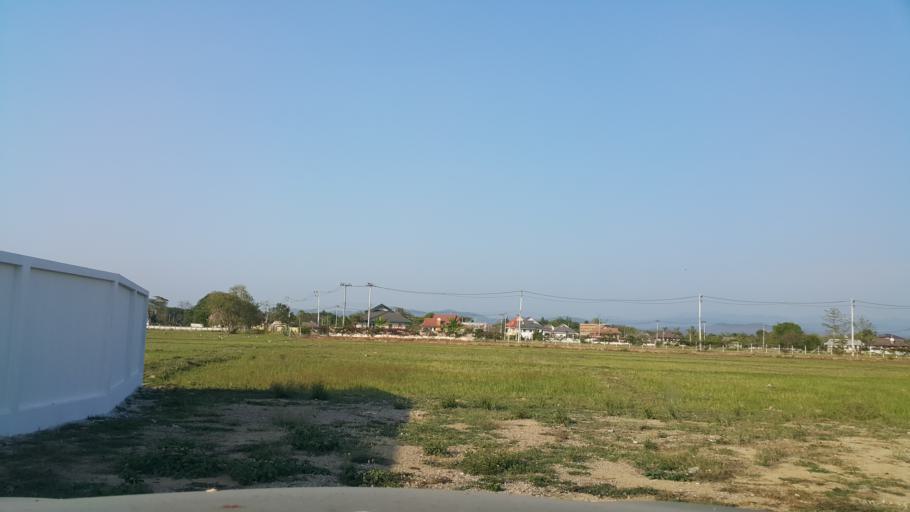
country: TH
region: Chiang Mai
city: San Sai
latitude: 18.8371
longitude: 99.0939
